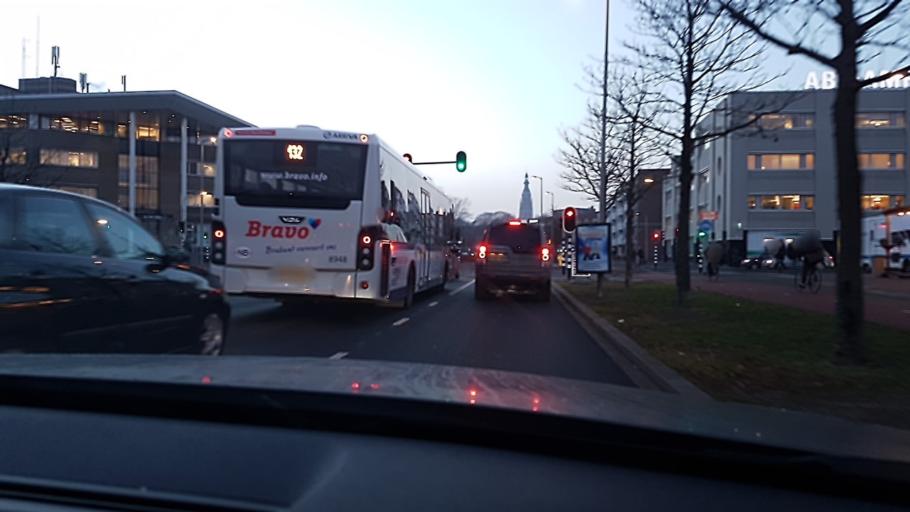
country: NL
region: North Brabant
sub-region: Gemeente Breda
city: Breda
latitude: 51.5875
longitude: 4.7853
